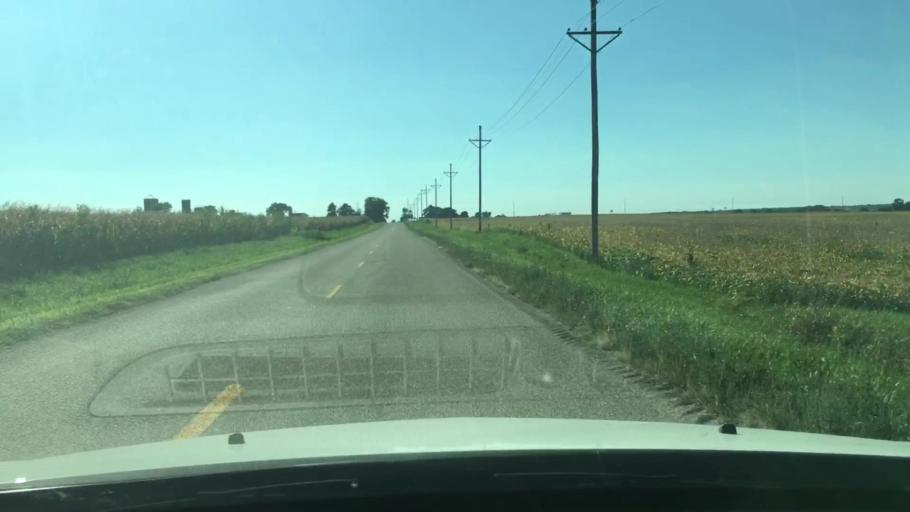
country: US
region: Illinois
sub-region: Ogle County
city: Rochelle
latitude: 41.8987
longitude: -88.9867
